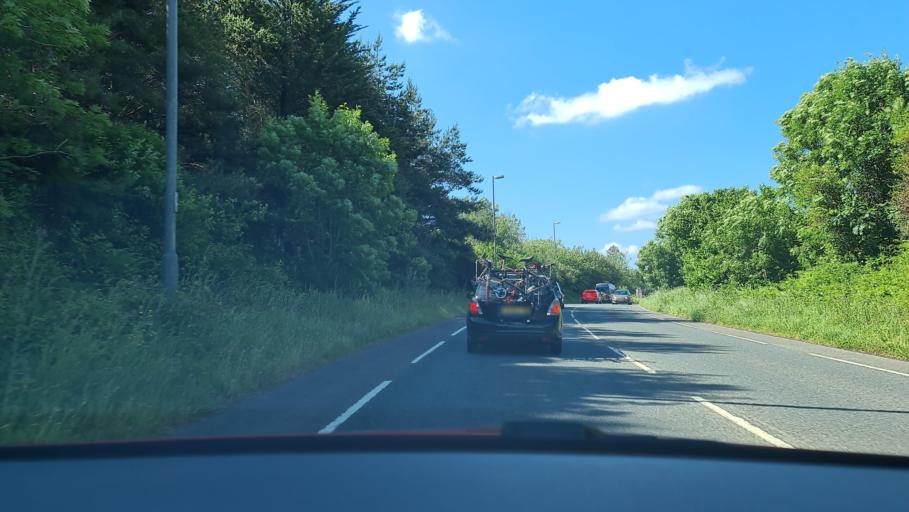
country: GB
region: England
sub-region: Cornwall
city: Liskeard
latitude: 50.4521
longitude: -4.4494
